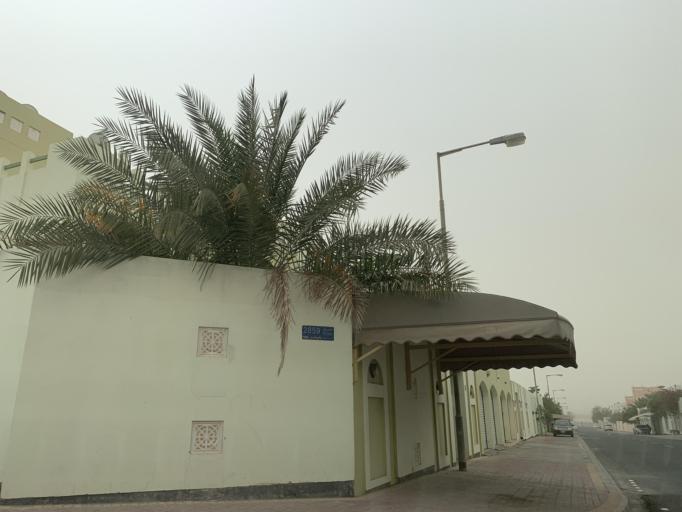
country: BH
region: Central Governorate
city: Madinat Hamad
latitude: 26.1267
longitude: 50.5106
